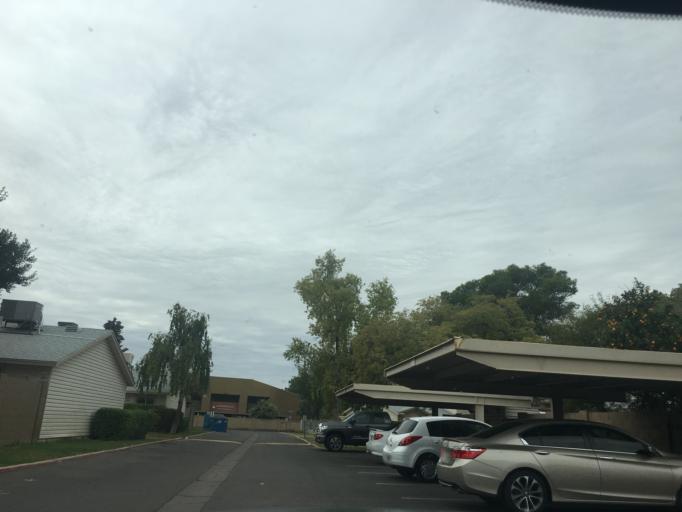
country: US
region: Arizona
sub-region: Maricopa County
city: Tempe
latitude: 33.3798
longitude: -111.9187
